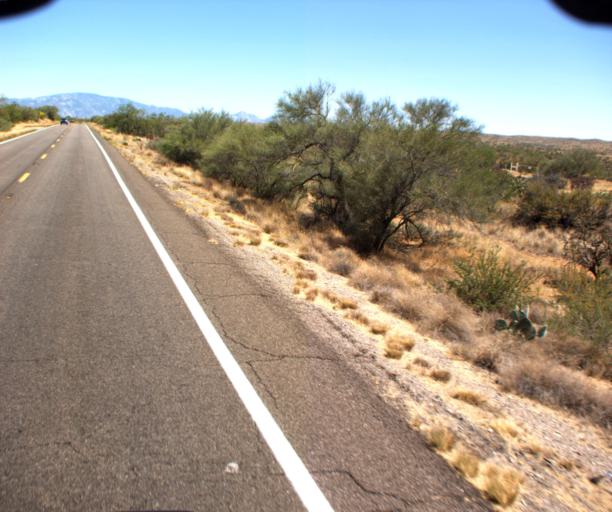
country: US
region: Arizona
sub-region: Pima County
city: Catalina
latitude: 32.6375
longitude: -111.0108
